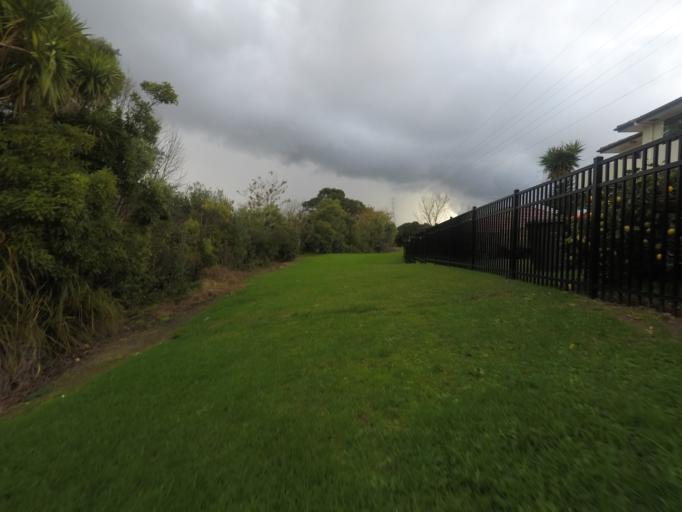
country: NZ
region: Auckland
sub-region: Auckland
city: Rosebank
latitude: -36.9014
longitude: 174.6870
